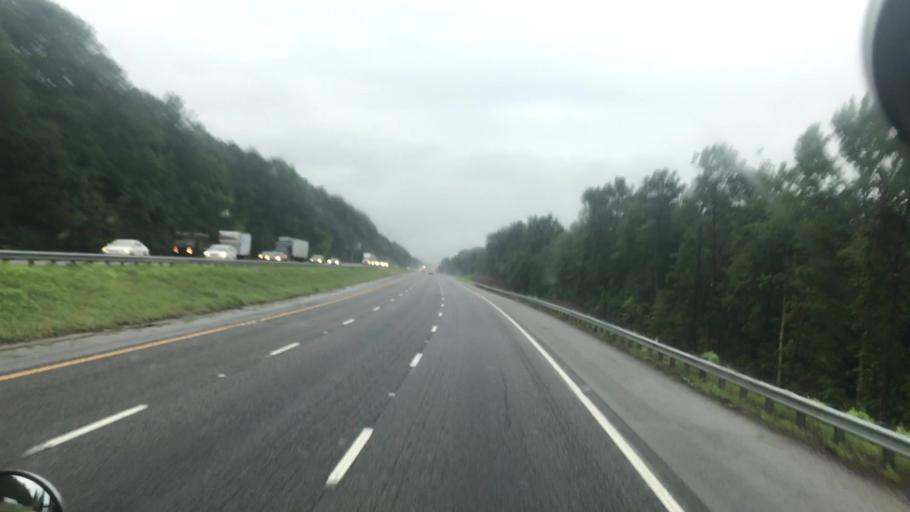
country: US
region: Georgia
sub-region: Monroe County
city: Forsyth
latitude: 33.1263
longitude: -84.0074
